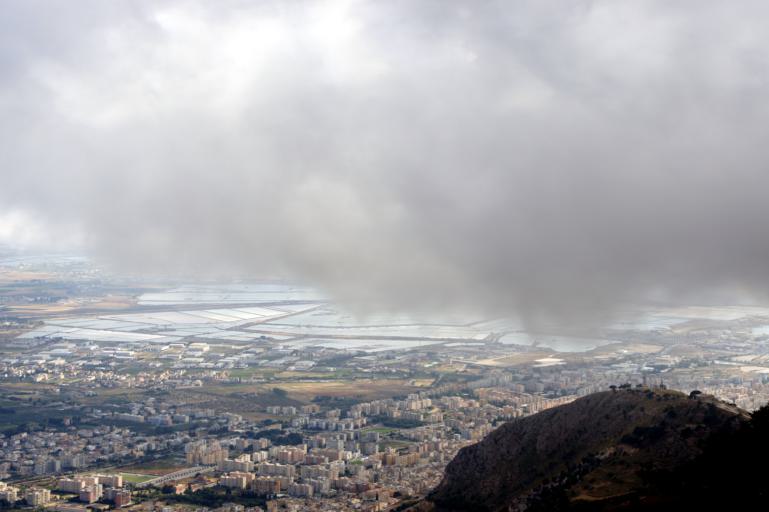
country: IT
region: Sicily
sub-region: Trapani
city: Erice
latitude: 38.0354
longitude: 12.5917
